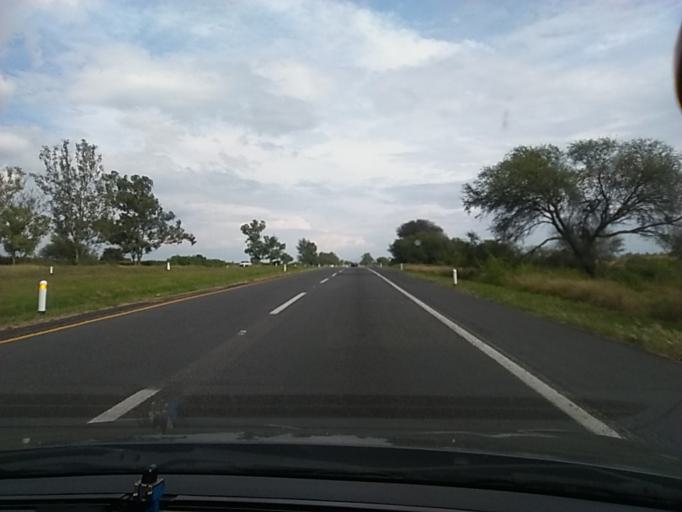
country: MX
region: Jalisco
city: Jamay
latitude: 20.3471
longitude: -102.6260
